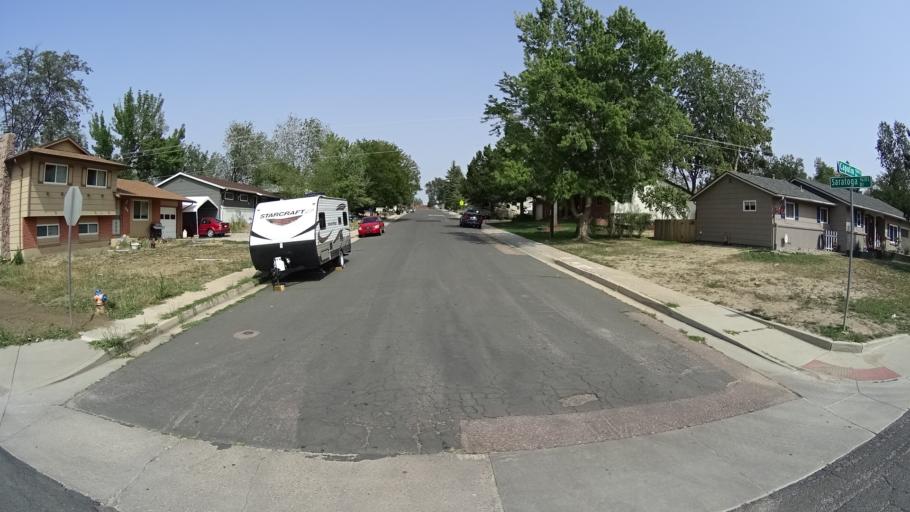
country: US
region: Colorado
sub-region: El Paso County
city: Stratmoor
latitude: 38.8088
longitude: -104.7736
